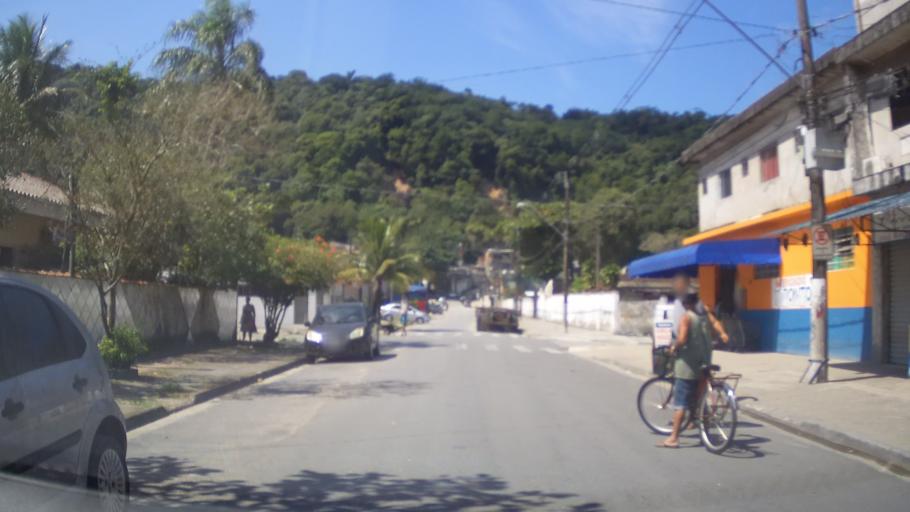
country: BR
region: Sao Paulo
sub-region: Praia Grande
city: Praia Grande
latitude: -23.9901
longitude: -46.3943
